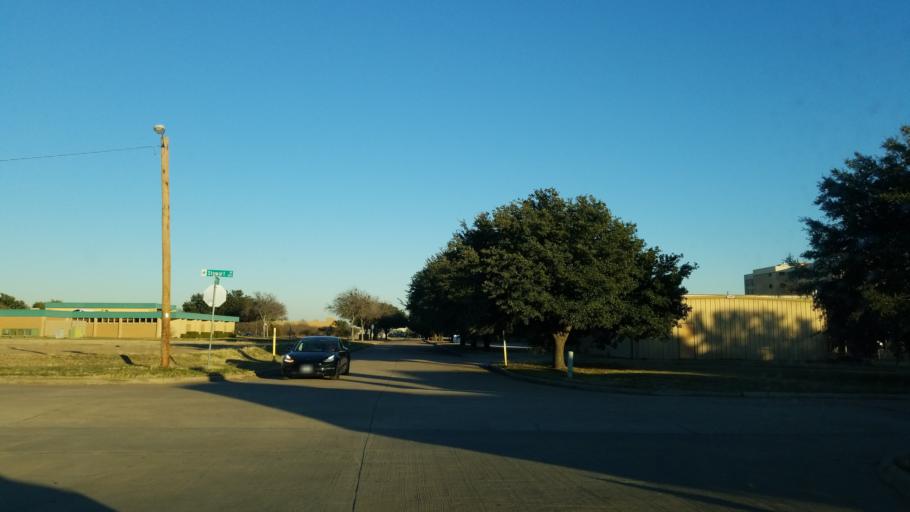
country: US
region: Texas
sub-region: Dallas County
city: Grand Prairie
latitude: 32.7338
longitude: -97.0515
